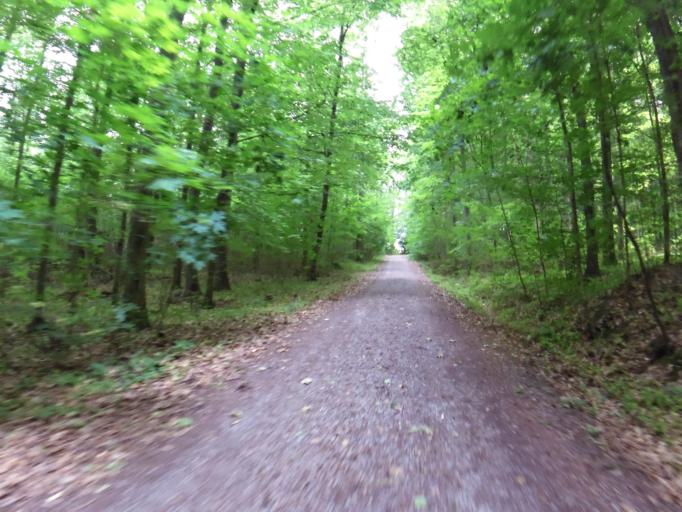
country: DE
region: Bavaria
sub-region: Regierungsbezirk Unterfranken
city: Zell am Main
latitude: 49.8206
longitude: 9.8516
